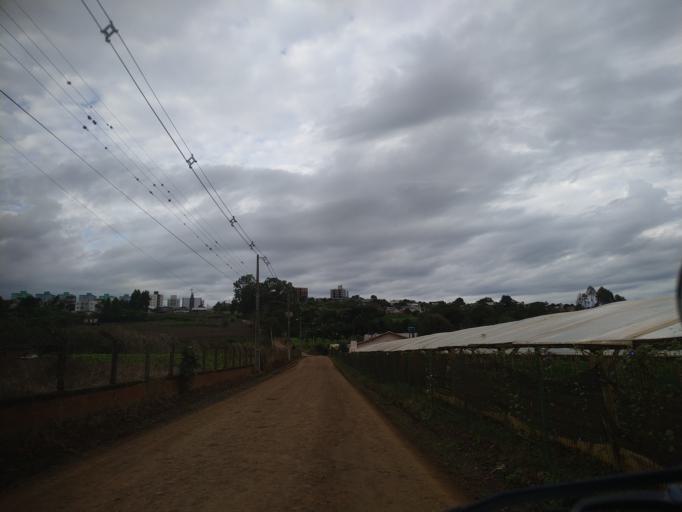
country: BR
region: Santa Catarina
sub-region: Chapeco
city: Chapeco
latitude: -27.0649
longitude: -52.6126
